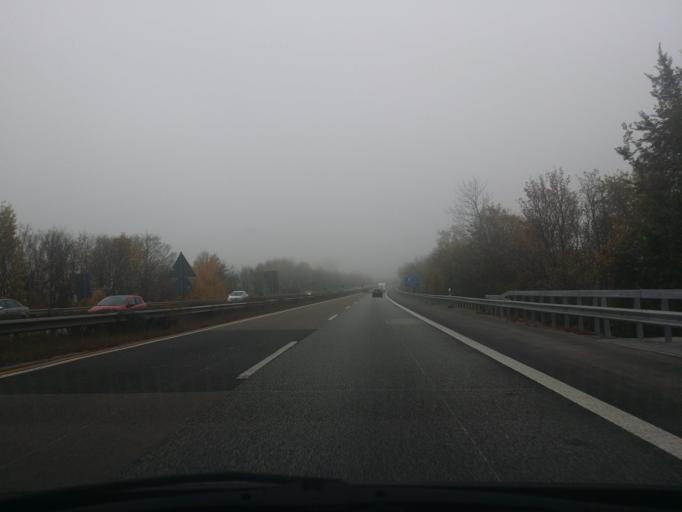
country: DE
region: Rheinland-Pfalz
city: Spiesheim
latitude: 49.8072
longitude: 8.1443
